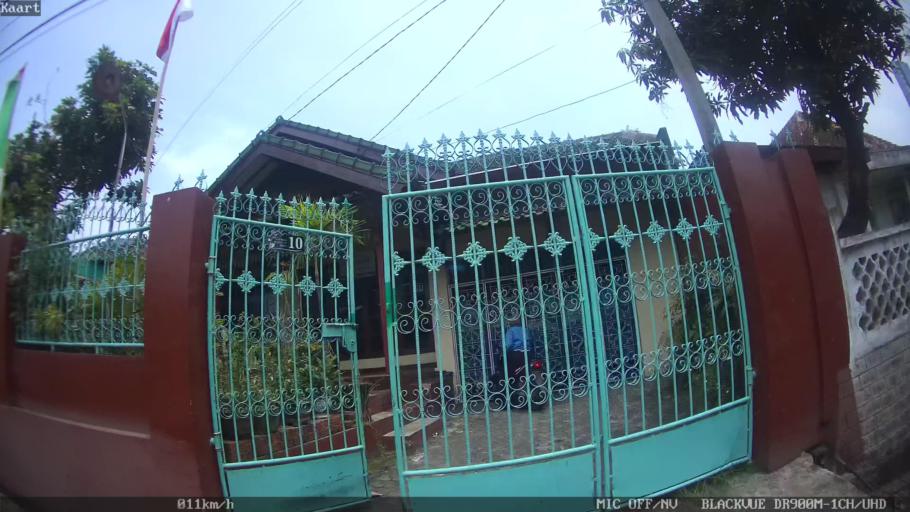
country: ID
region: Lampung
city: Bandarlampung
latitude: -5.4155
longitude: 105.2627
